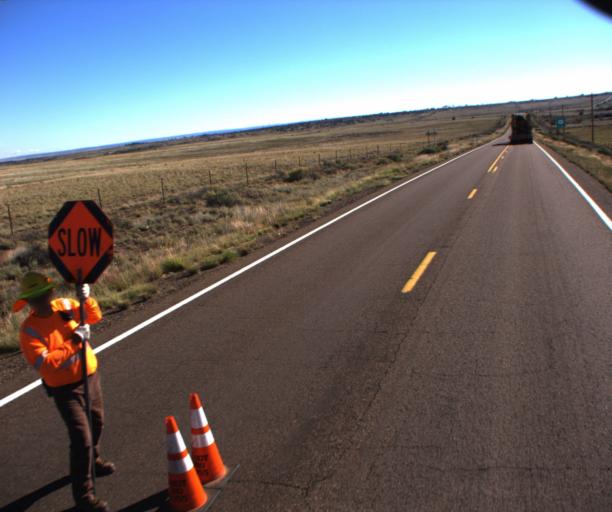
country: US
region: Arizona
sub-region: Apache County
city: Saint Johns
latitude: 34.5103
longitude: -109.4579
